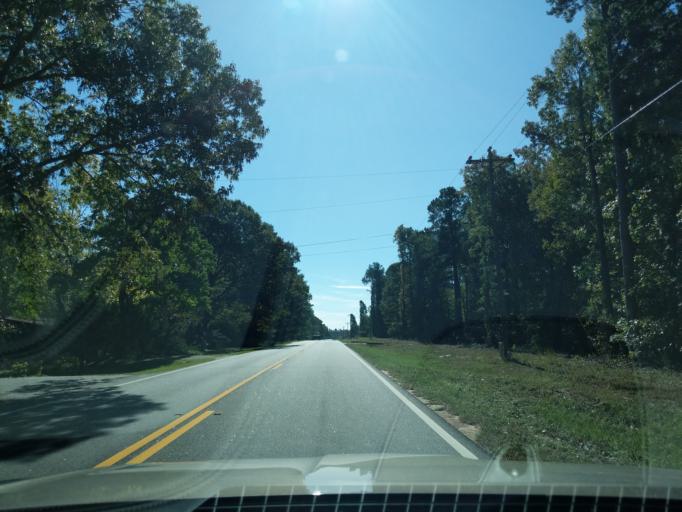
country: US
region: Georgia
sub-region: Richmond County
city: Hephzibah
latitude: 33.2747
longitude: -82.0142
